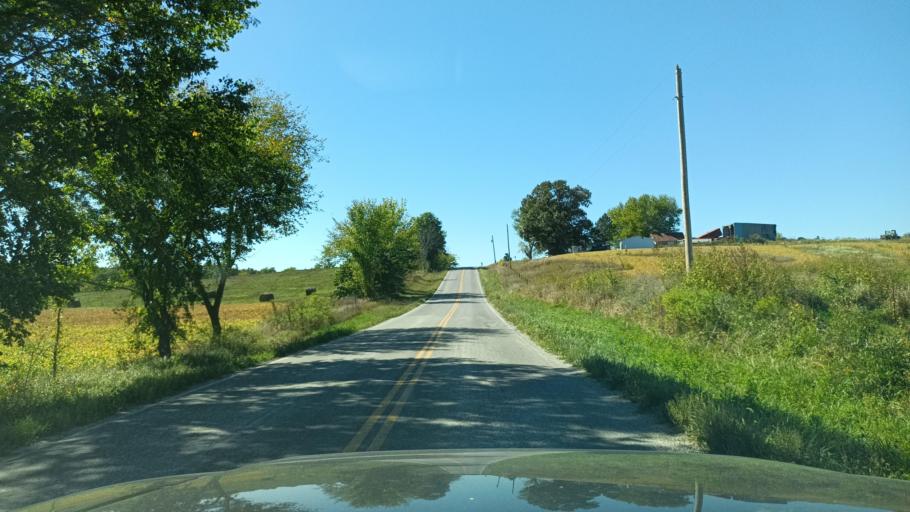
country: US
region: Missouri
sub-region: Macon County
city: La Plata
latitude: 40.0217
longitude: -92.5329
